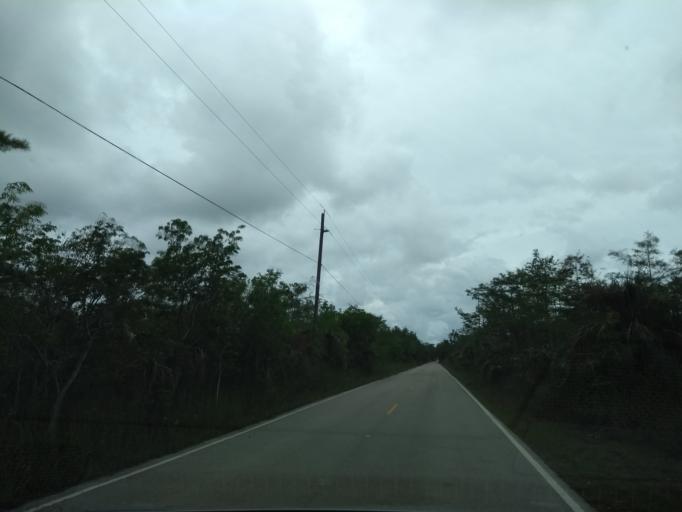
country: US
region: Florida
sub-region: Miami-Dade County
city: The Hammocks
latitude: 25.7464
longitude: -80.9429
